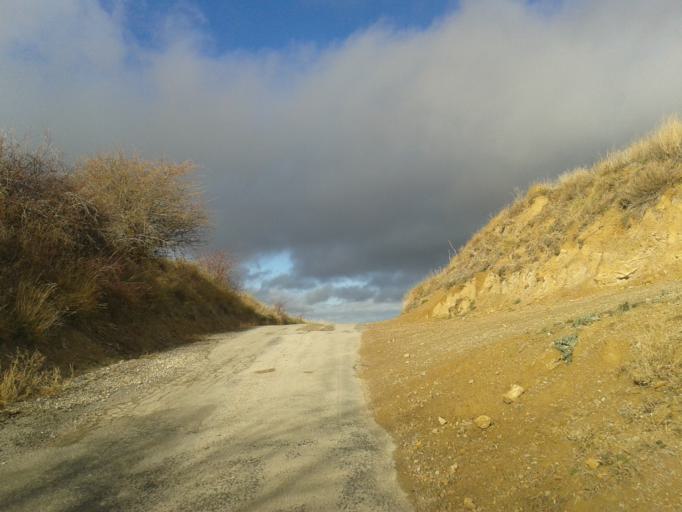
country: ES
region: Aragon
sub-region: Provincia de Teruel
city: Bea
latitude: 40.9855
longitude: -1.1627
